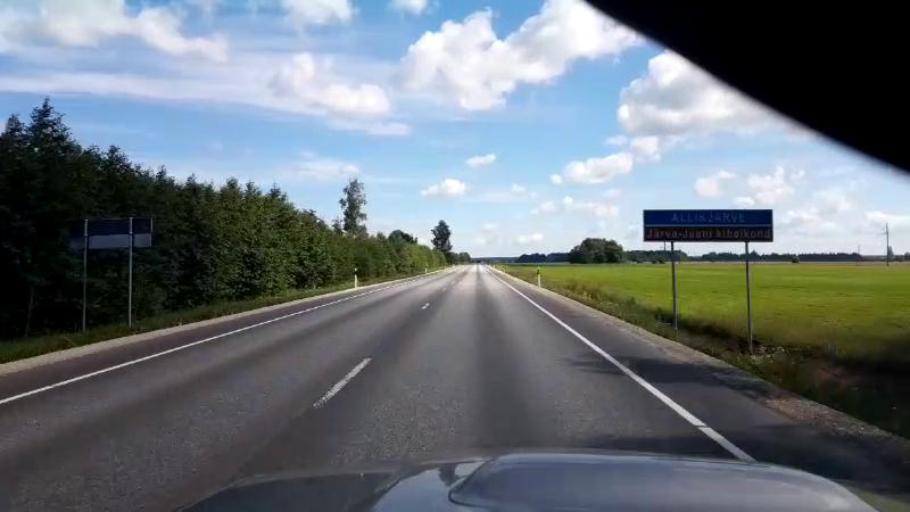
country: EE
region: Jaervamaa
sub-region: Paide linn
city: Paide
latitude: 59.0062
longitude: 25.6851
